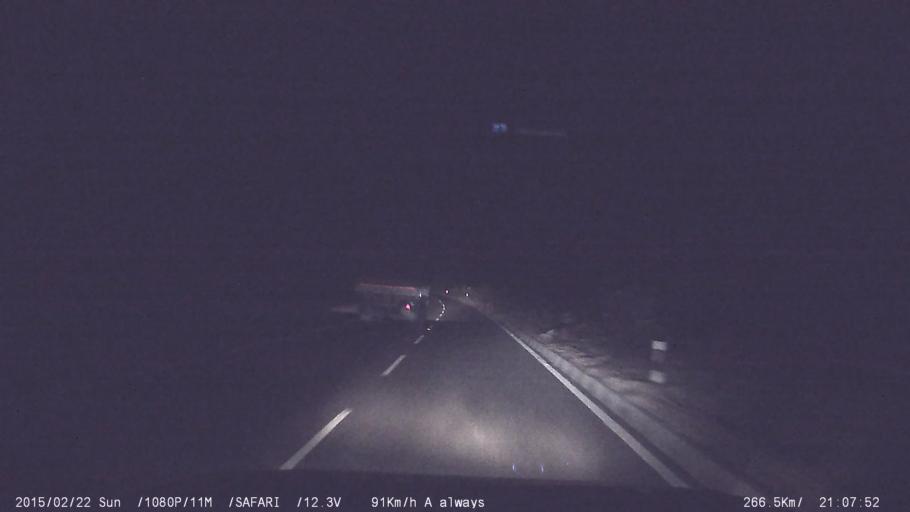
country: IN
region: Tamil Nadu
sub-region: Karur
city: Pallappatti
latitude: 10.7274
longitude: 77.9266
